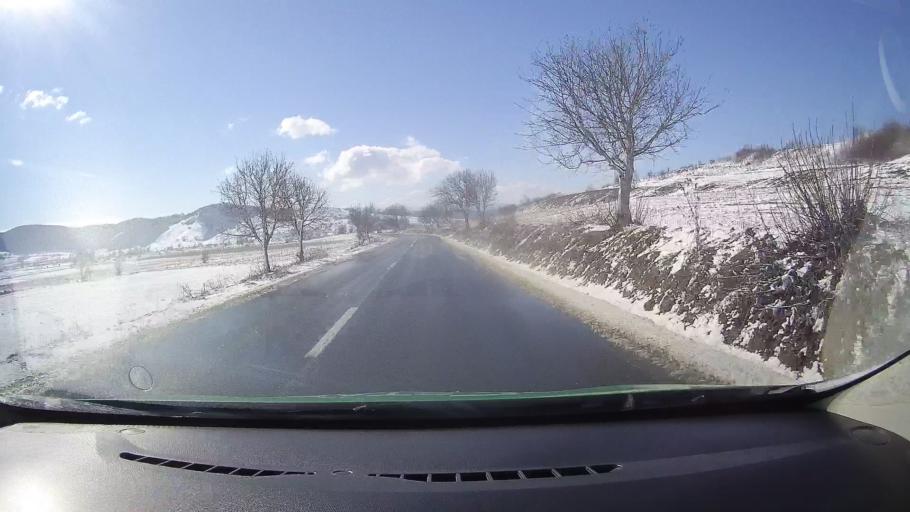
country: RO
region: Sibiu
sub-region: Comuna Rosia
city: Rosia
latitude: 45.7989
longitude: 24.3430
